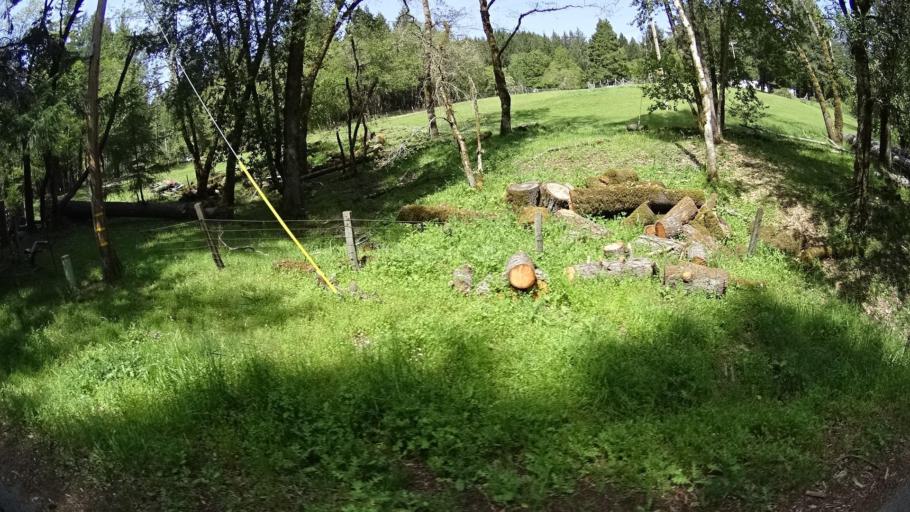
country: US
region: California
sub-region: Humboldt County
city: Redway
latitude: 40.3489
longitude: -123.7137
